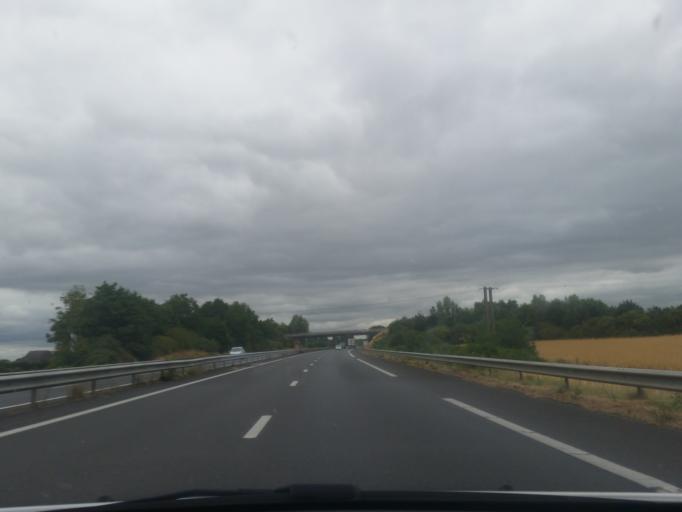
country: FR
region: Pays de la Loire
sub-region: Departement de la Sarthe
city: Noyen-sur-Sarthe
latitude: 47.8768
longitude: -0.1173
